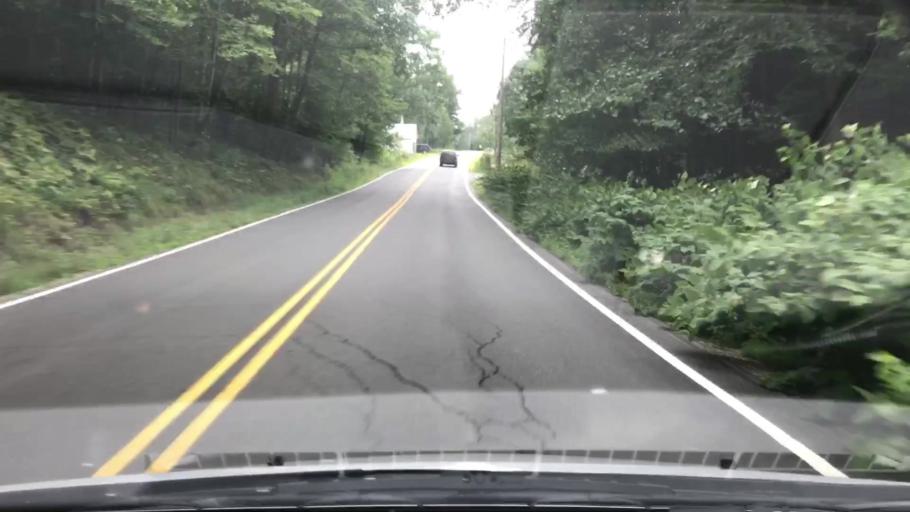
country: US
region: New Hampshire
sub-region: Grafton County
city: Woodsville
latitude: 44.1821
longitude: -72.0507
